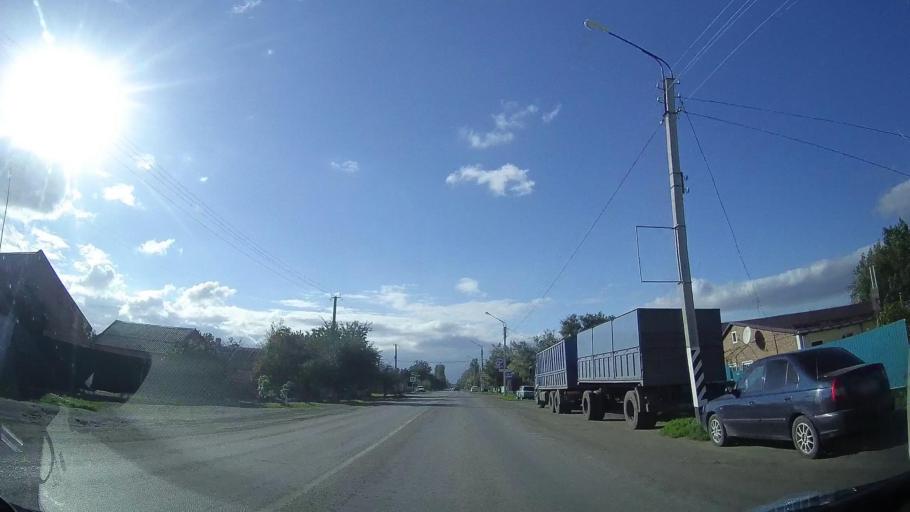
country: RU
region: Rostov
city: Tselina
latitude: 46.5309
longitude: 41.0197
